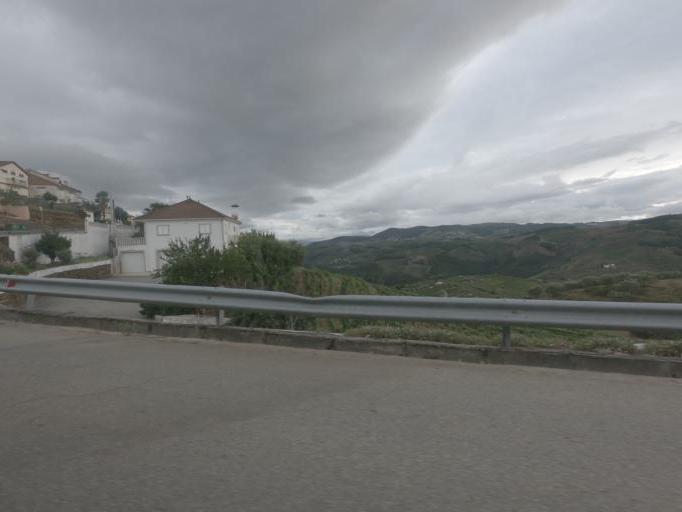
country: PT
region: Vila Real
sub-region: Sabrosa
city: Sabrosa
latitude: 41.2803
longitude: -7.5376
